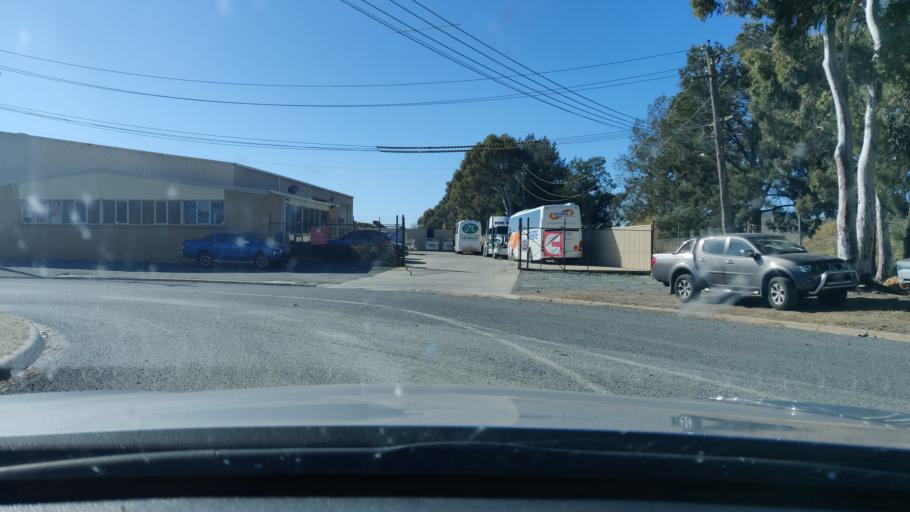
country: AU
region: Australian Capital Territory
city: Macarthur
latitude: -35.3884
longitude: 149.1745
